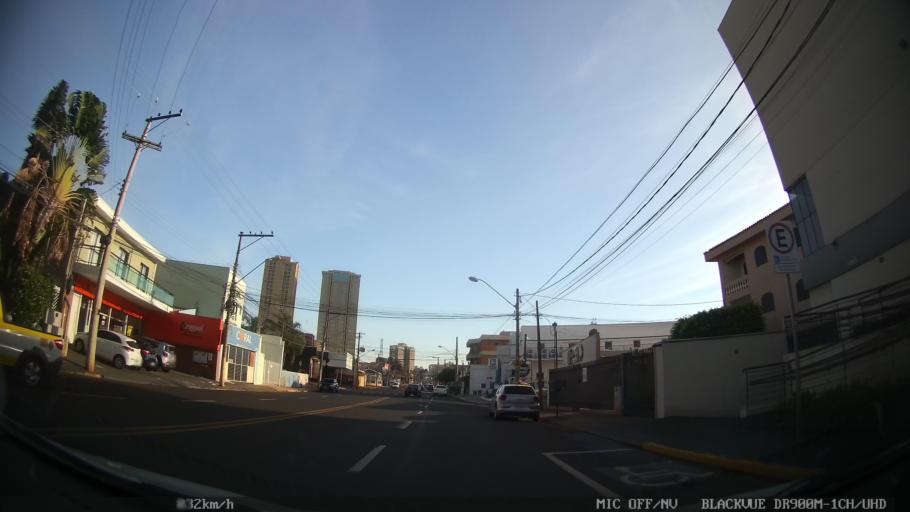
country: BR
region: Sao Paulo
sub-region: Ribeirao Preto
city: Ribeirao Preto
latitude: -21.1962
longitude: -47.8003
